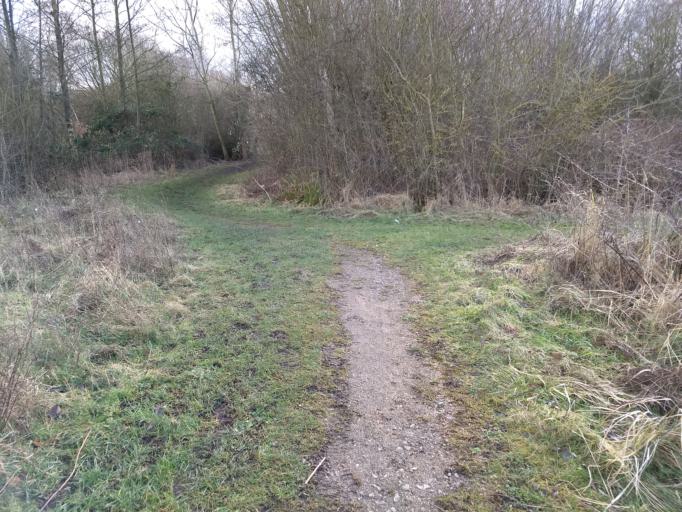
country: GB
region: England
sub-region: Buckinghamshire
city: Bletchley
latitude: 51.9857
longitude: -0.7382
